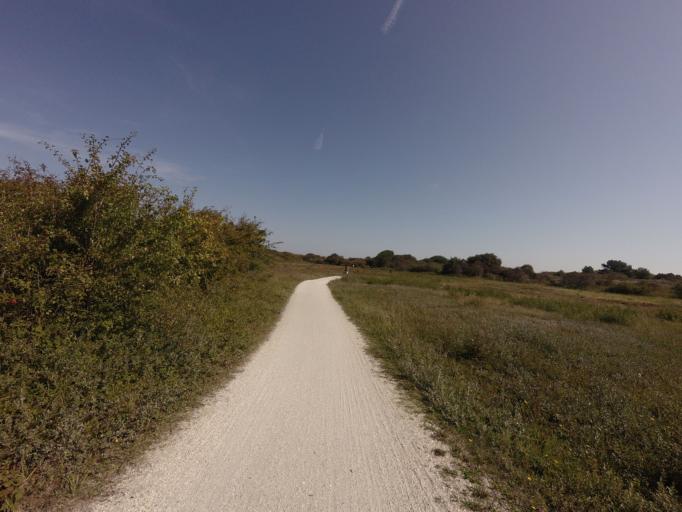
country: NL
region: Friesland
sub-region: Gemeente Schiermonnikoog
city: Schiermonnikoog
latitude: 53.4829
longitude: 6.1460
